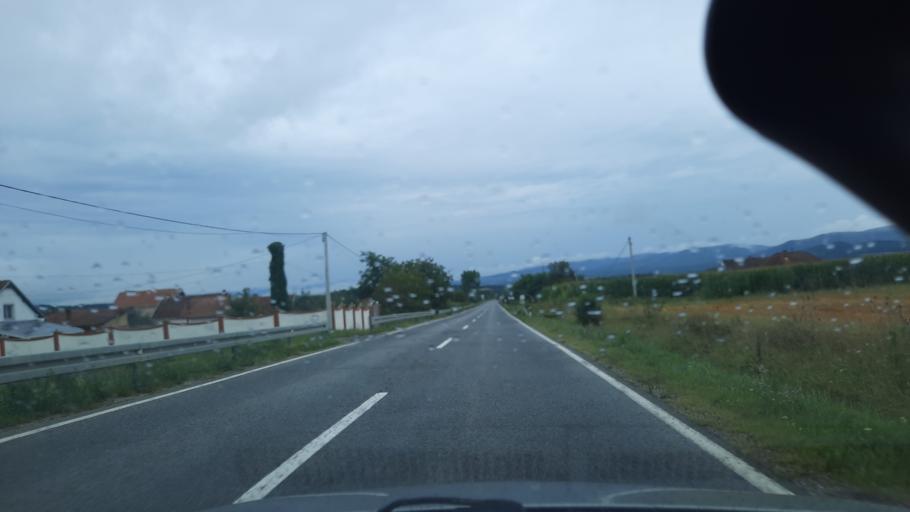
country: RS
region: Central Serbia
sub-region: Sumadijski Okrug
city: Knic
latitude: 43.9269
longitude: 20.7741
